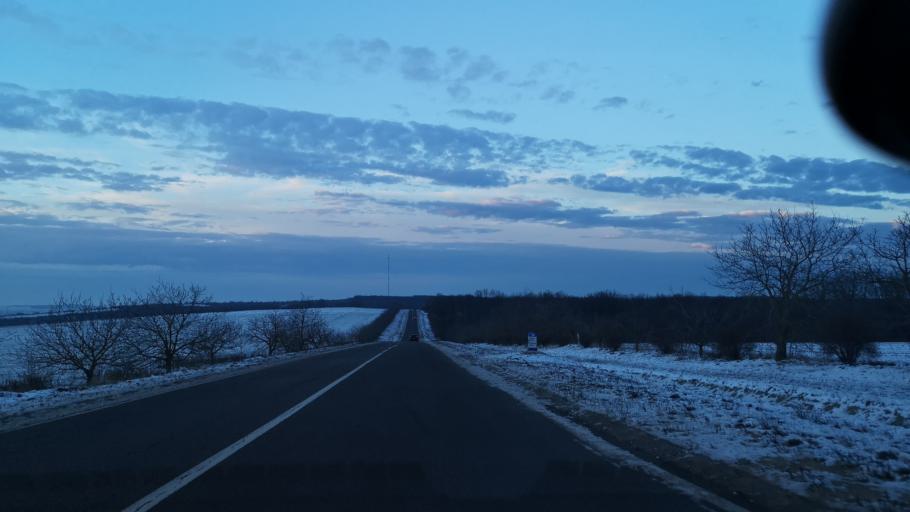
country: MD
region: Rezina
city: Saharna
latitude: 47.6357
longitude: 28.8365
